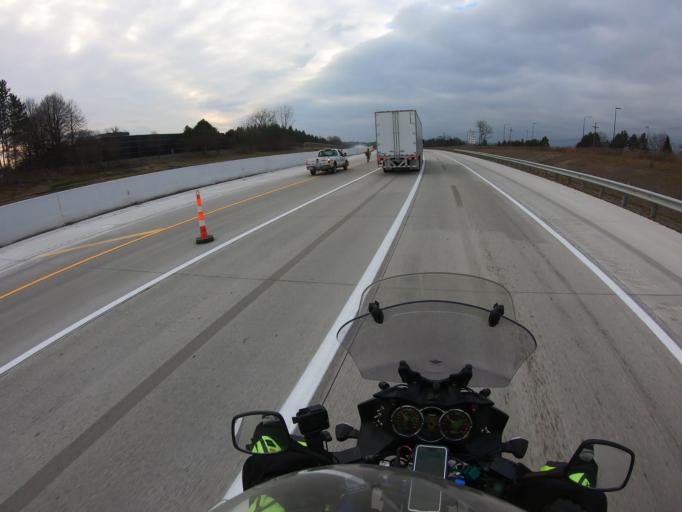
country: US
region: Michigan
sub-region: Oakland County
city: Troy
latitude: 42.6079
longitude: -83.1749
